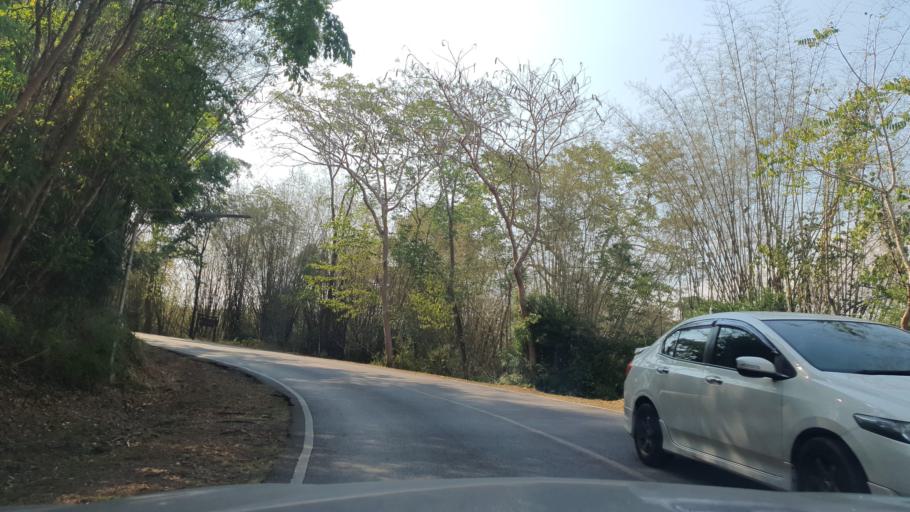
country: TH
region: Kanchanaburi
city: Si Sawat
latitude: 14.3797
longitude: 99.1412
